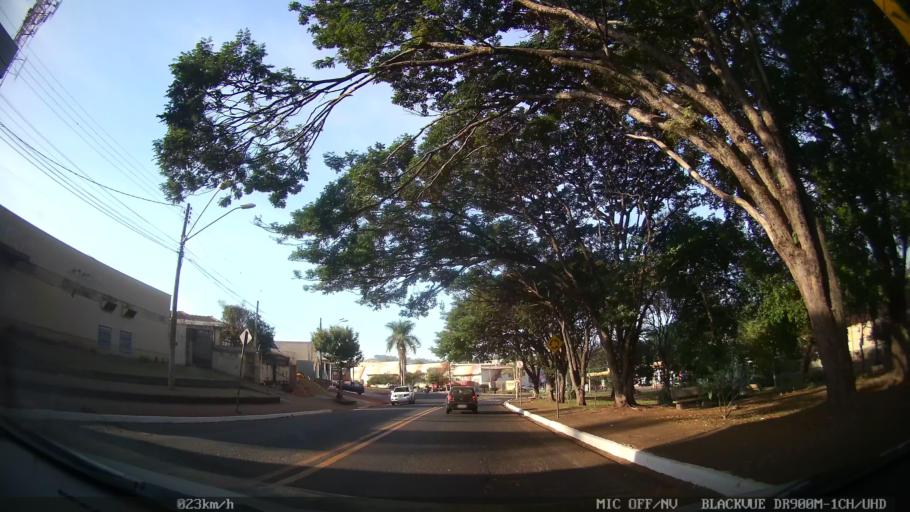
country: BR
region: Sao Paulo
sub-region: Ribeirao Preto
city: Ribeirao Preto
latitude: -21.2666
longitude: -47.8177
